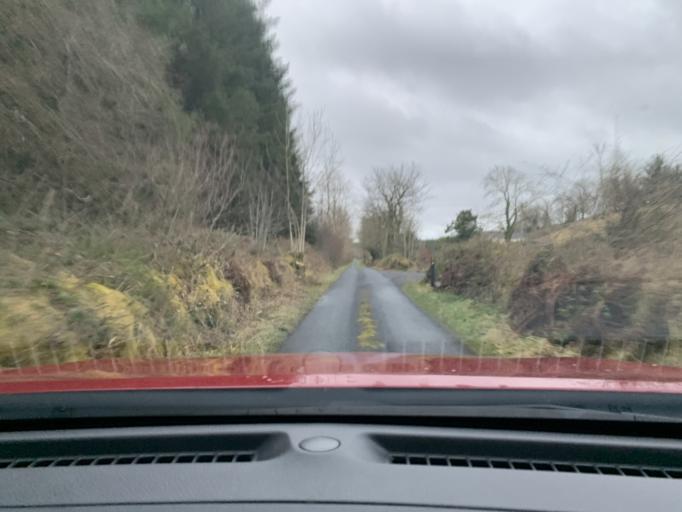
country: IE
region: Connaught
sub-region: Roscommon
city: Boyle
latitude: 54.0050
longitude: -8.3808
